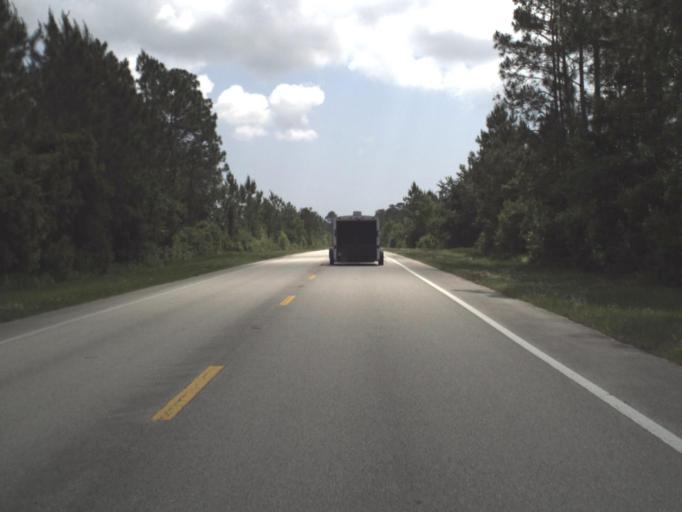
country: US
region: Florida
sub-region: Saint Johns County
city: Saint Augustine Shores
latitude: 29.7425
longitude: -81.3599
